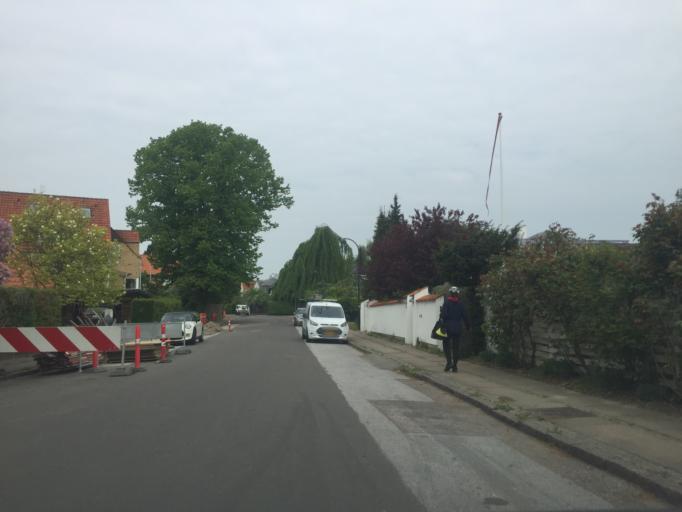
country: DK
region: Capital Region
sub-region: Gentofte Kommune
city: Charlottenlund
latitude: 55.7555
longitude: 12.5620
